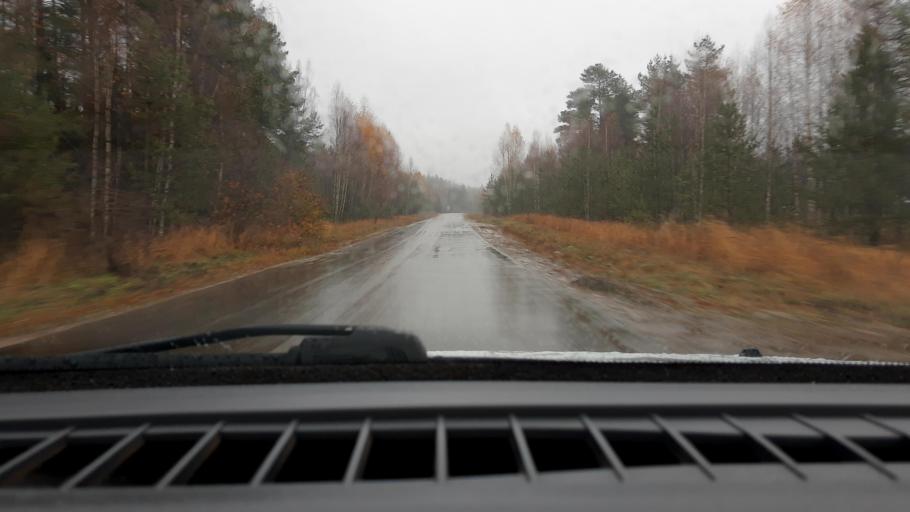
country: RU
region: Nizjnij Novgorod
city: Linda
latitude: 56.6940
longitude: 44.2048
